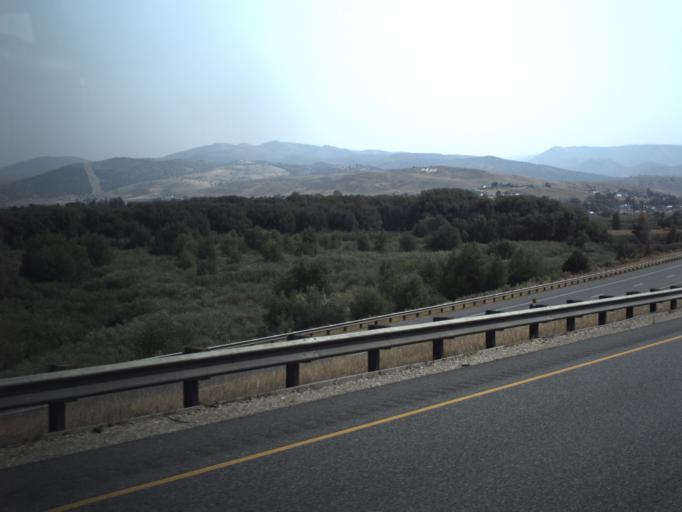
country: US
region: Utah
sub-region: Summit County
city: Coalville
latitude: 40.9212
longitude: -111.4102
